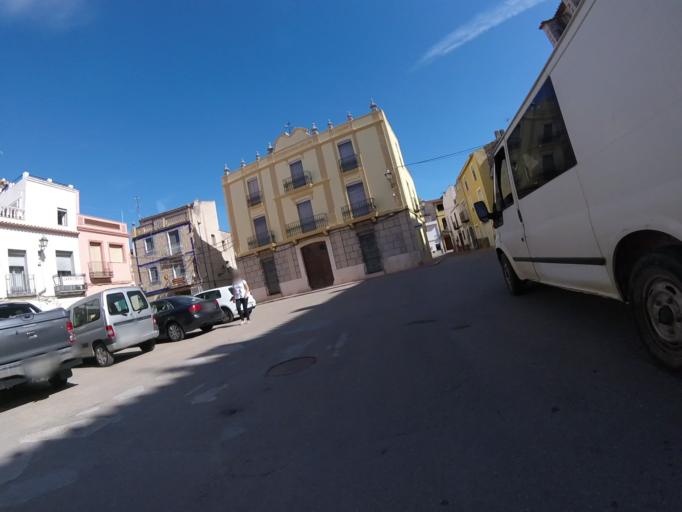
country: ES
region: Valencia
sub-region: Provincia de Castello
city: Santa Magdalena de Pulpis
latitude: 40.3562
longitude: 0.3029
